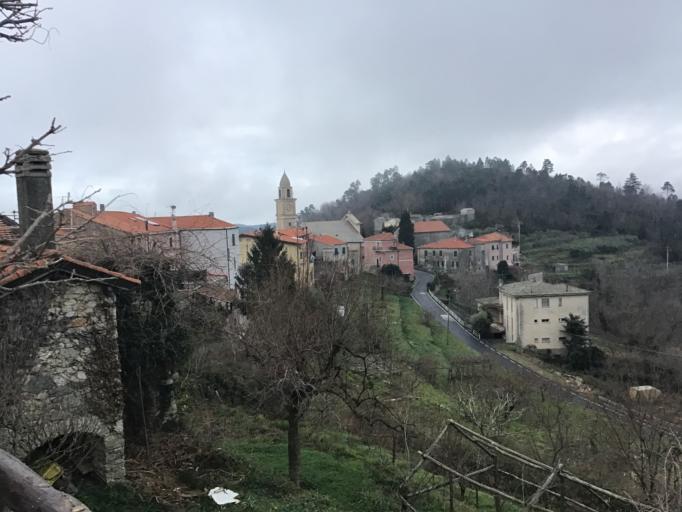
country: IT
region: Liguria
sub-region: Provincia di Savona
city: Orco Feglino
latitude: 44.2237
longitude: 8.3437
